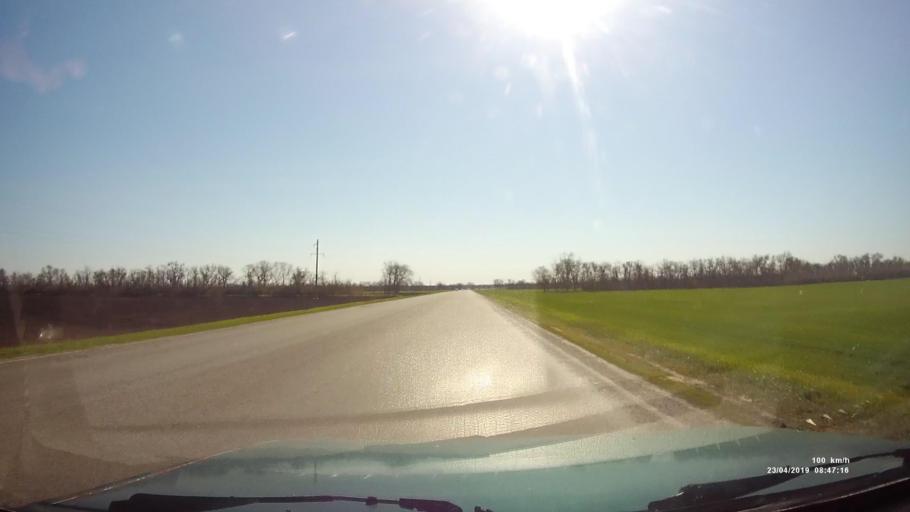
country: RU
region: Rostov
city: Gigant
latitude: 46.5156
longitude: 41.3667
